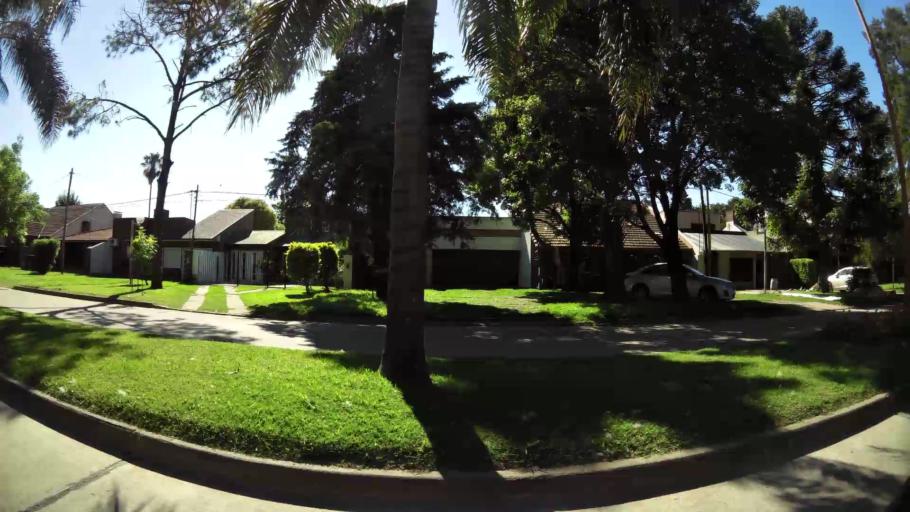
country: AR
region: Santa Fe
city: Esperanza
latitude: -31.4464
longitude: -60.9175
